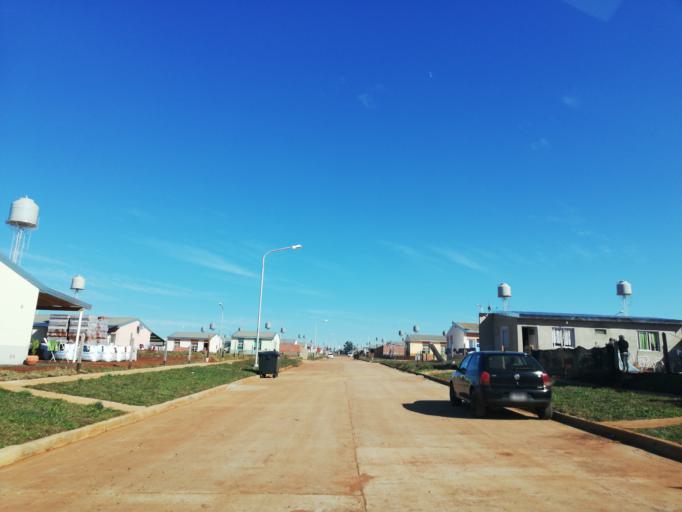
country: AR
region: Misiones
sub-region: Departamento de Capital
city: Posadas
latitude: -27.4113
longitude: -55.9897
